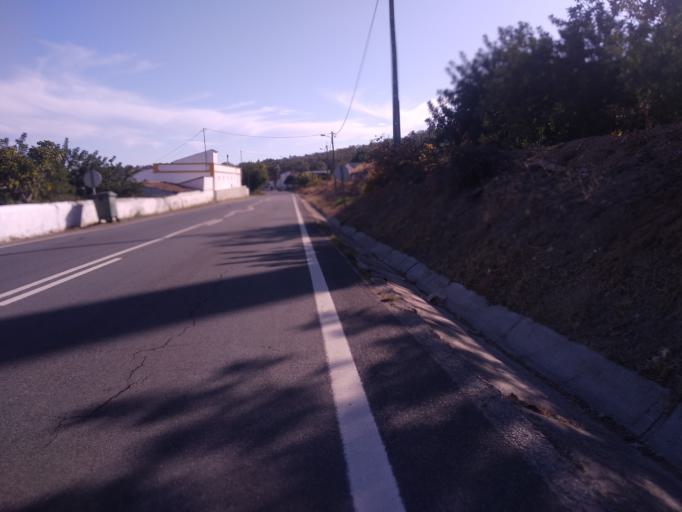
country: PT
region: Faro
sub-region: Sao Bras de Alportel
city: Sao Bras de Alportel
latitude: 37.1150
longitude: -7.9075
